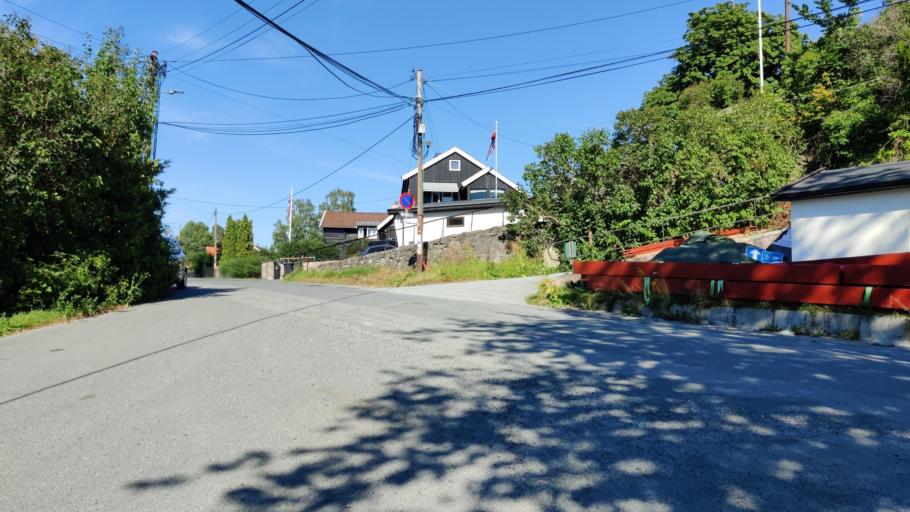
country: NO
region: Akershus
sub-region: Baerum
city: Lysaker
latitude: 59.9199
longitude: 10.5913
